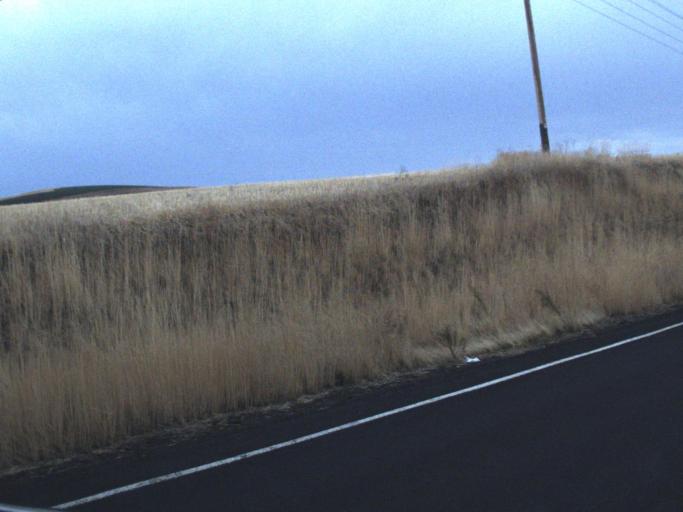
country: US
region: Washington
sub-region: Lincoln County
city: Davenport
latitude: 47.8411
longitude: -118.2128
